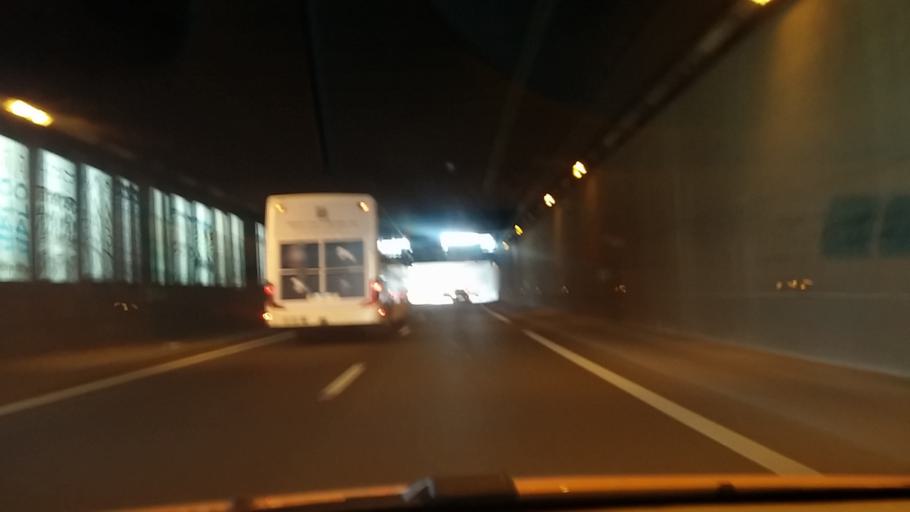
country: FR
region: Ile-de-France
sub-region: Departement du Val-de-Marne
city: Le Perreux-sur-Marne
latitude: 48.8478
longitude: 2.4912
